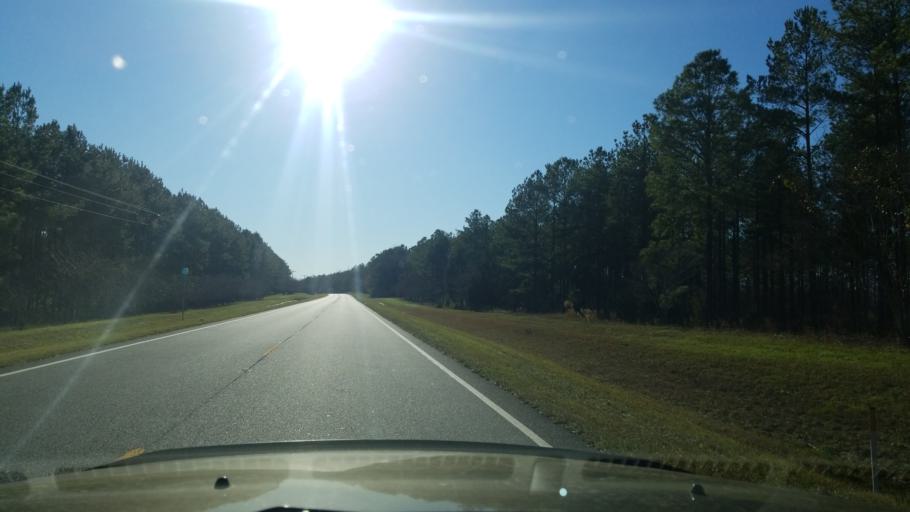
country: US
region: Georgia
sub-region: Talbot County
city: Talbotton
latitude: 32.6222
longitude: -84.5423
